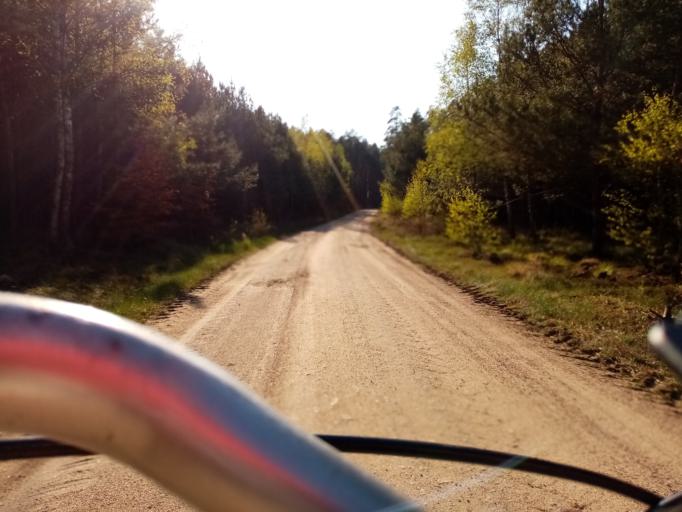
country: PL
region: Kujawsko-Pomorskie
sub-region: Powiat brodnicki
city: Gorzno
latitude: 53.1574
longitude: 19.6968
